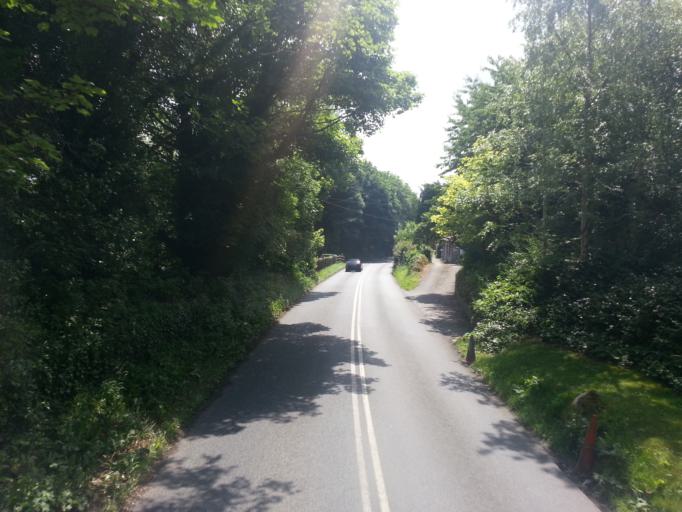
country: IE
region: Leinster
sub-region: Wicklow
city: Enniskerry
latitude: 53.2147
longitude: -6.1773
